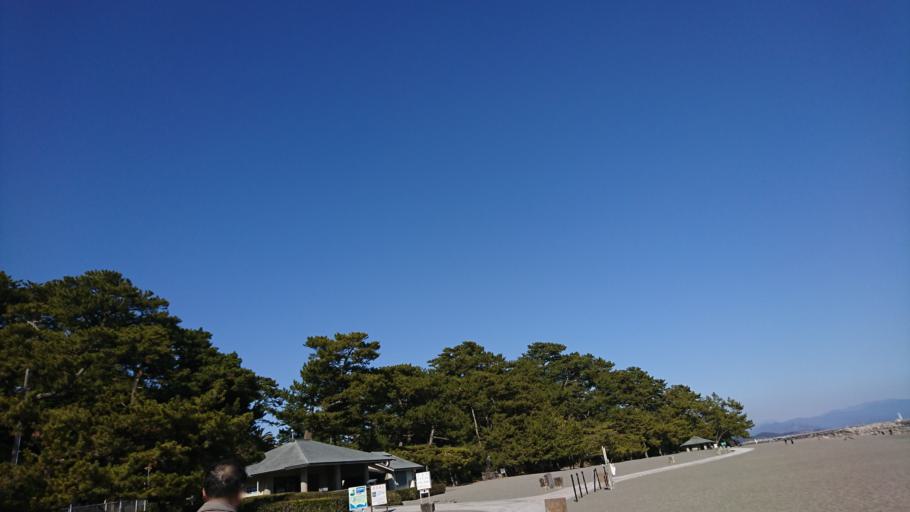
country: JP
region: Kochi
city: Kochi-shi
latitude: 33.4972
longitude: 133.5741
